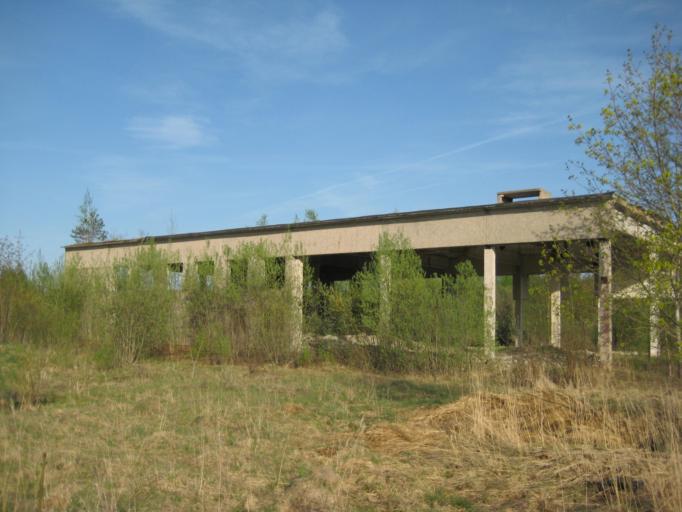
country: LT
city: Birstonas
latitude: 54.7507
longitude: 24.1054
